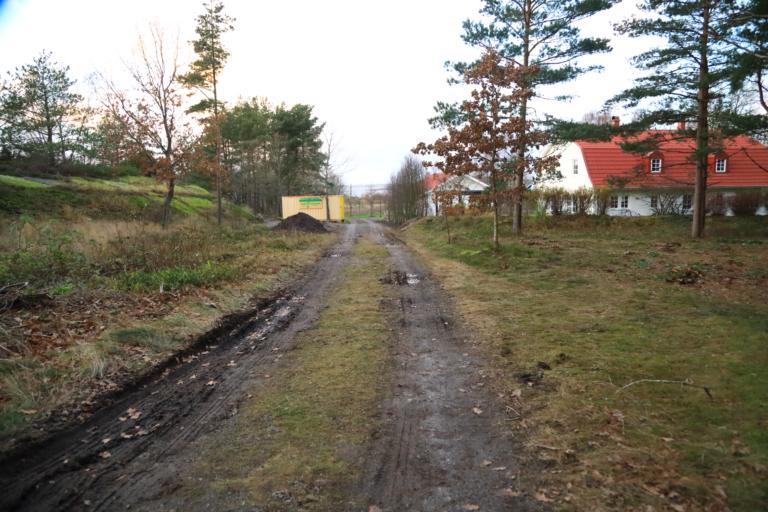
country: SE
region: Halland
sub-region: Varbergs Kommun
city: Varberg
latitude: 57.1480
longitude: 12.2213
